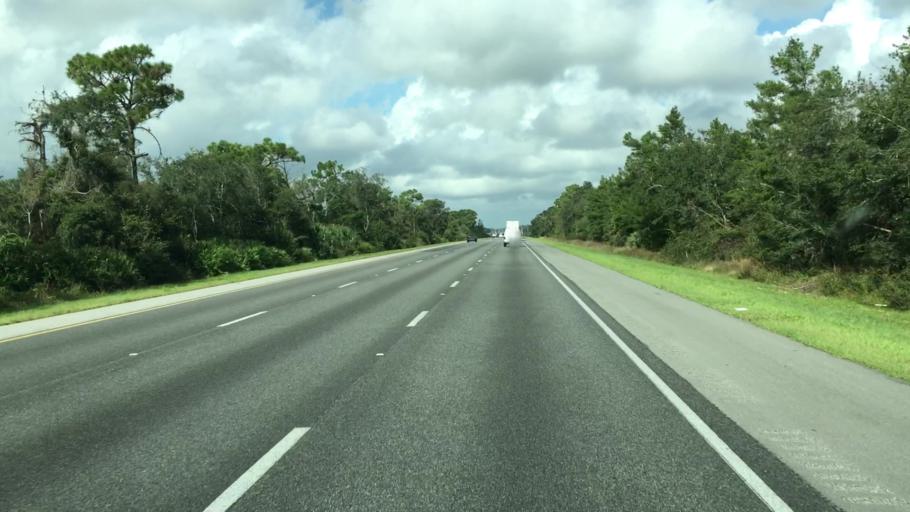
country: US
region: Florida
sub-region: Volusia County
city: Samsula-Spruce Creek
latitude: 29.0759
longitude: -81.0135
